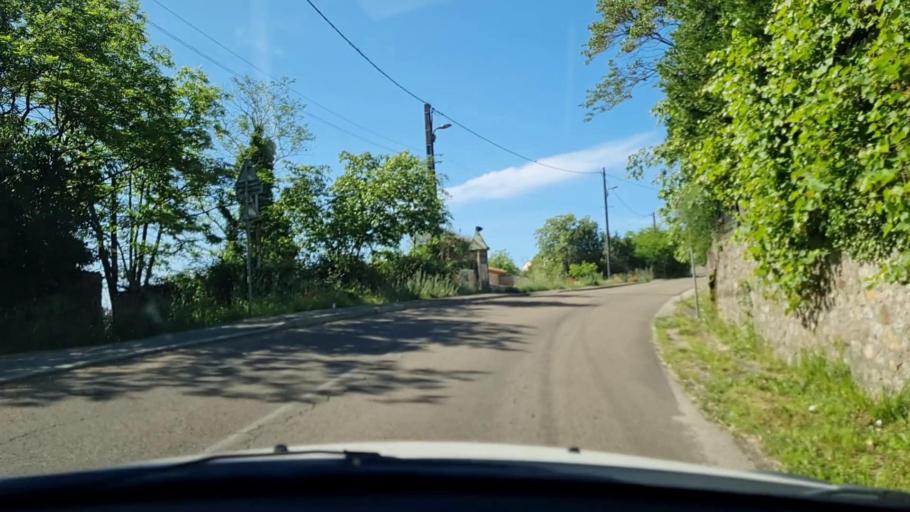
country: FR
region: Languedoc-Roussillon
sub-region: Departement du Gard
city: Cendras
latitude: 44.1424
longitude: 4.0749
